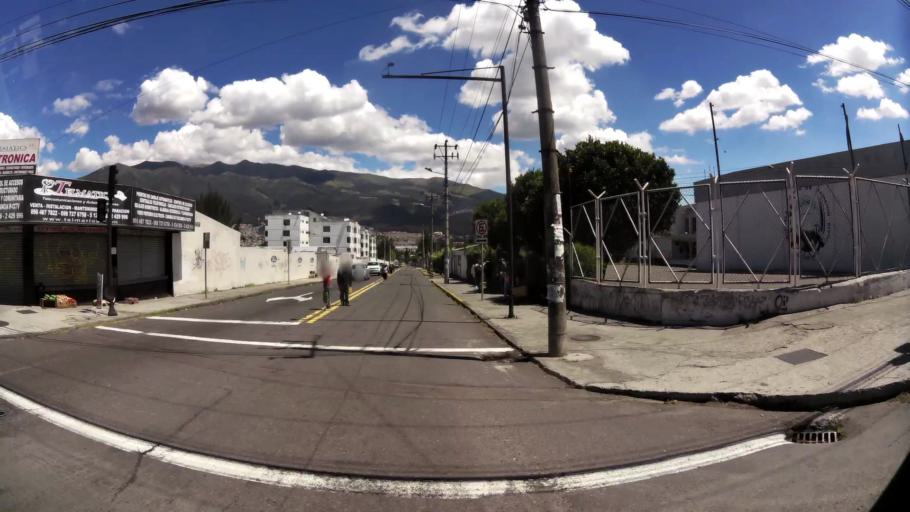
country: EC
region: Pichincha
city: Quito
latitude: -0.1357
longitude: -78.4822
